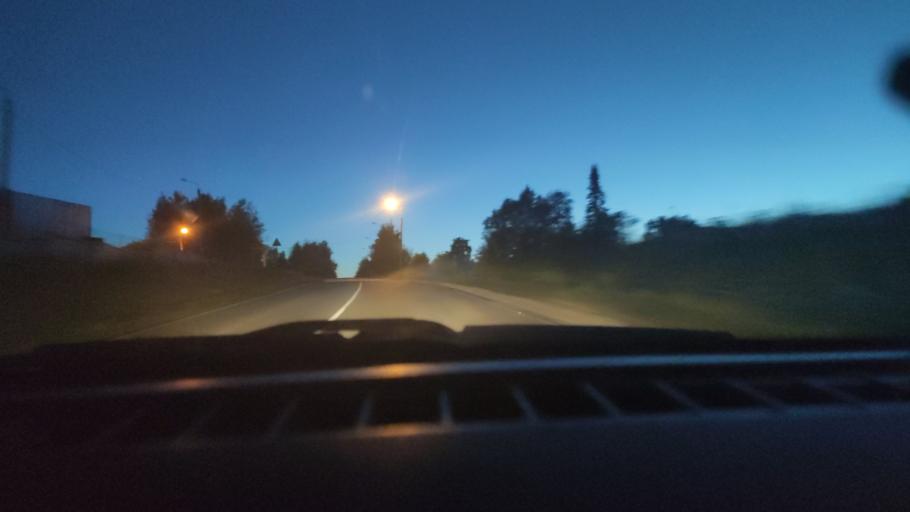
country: RU
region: Perm
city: Novyye Lyady
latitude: 58.0437
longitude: 56.5950
